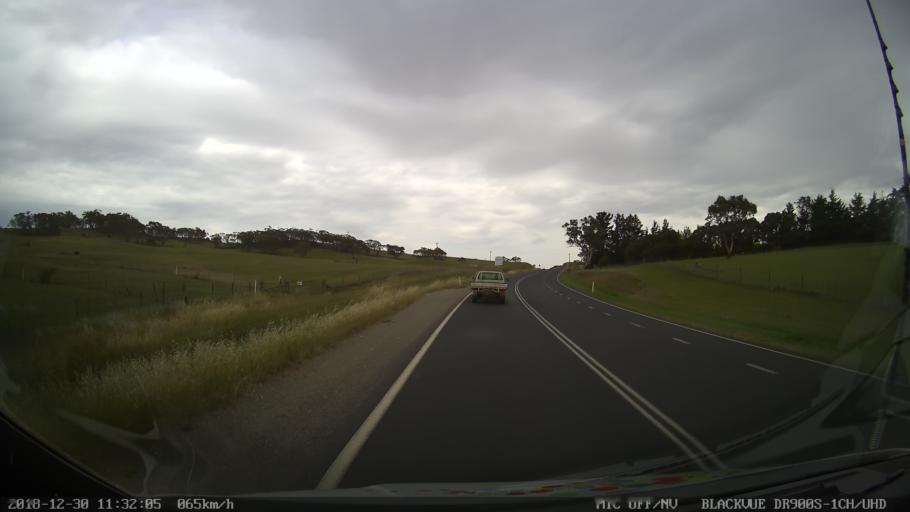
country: AU
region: New South Wales
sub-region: Snowy River
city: Jindabyne
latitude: -36.4248
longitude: 148.6091
